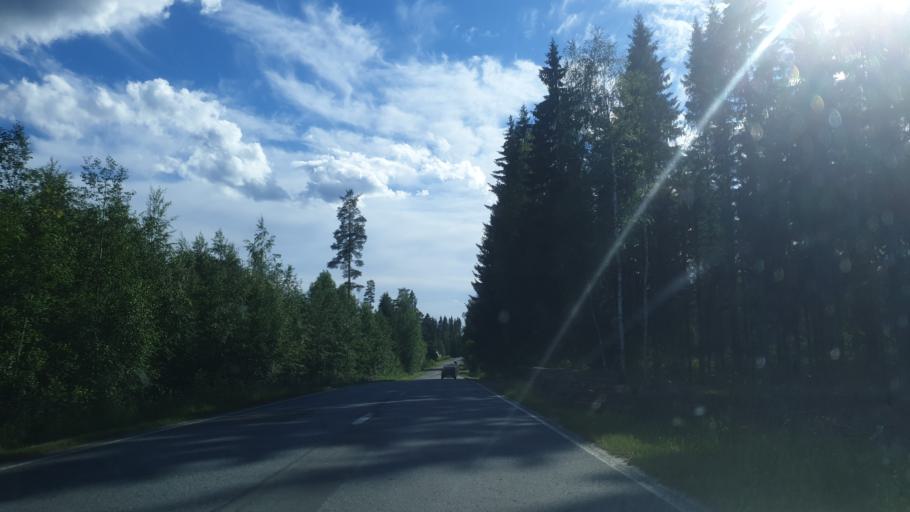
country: FI
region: Southern Savonia
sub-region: Mikkeli
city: Pertunmaa
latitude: 61.5216
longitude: 26.5024
